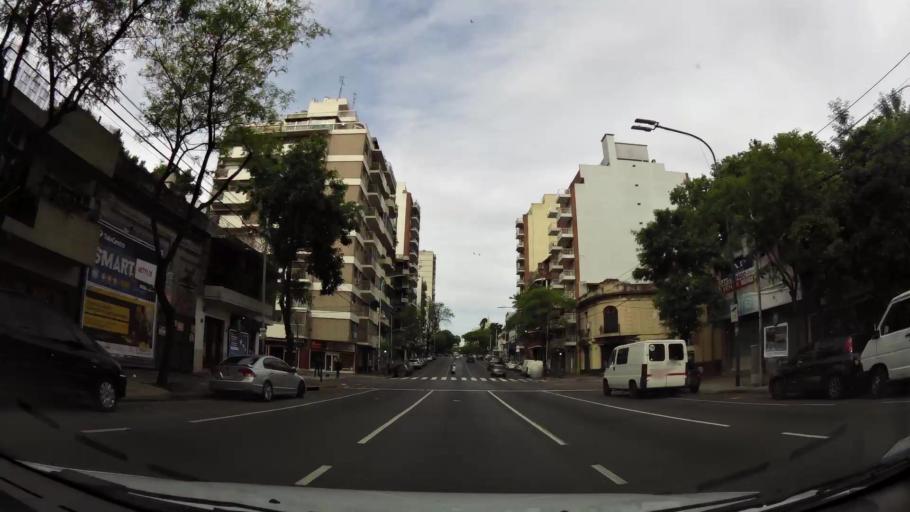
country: AR
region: Buenos Aires F.D.
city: Villa Santa Rita
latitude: -34.6330
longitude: -58.4593
